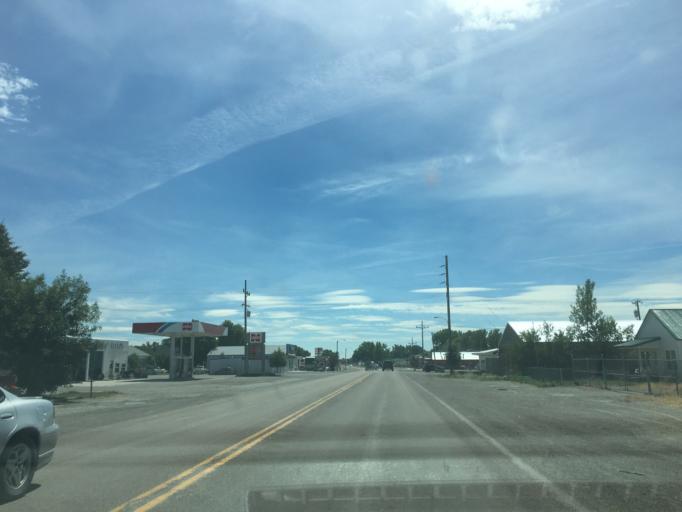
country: US
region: Montana
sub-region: Teton County
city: Choteau
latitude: 47.8089
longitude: -112.1808
